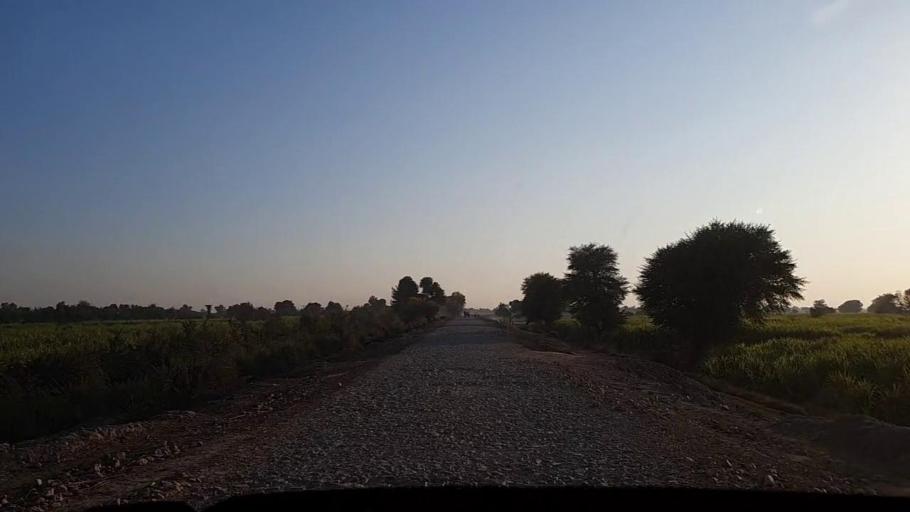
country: PK
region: Sindh
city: Sobhadero
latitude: 27.3723
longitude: 68.3784
